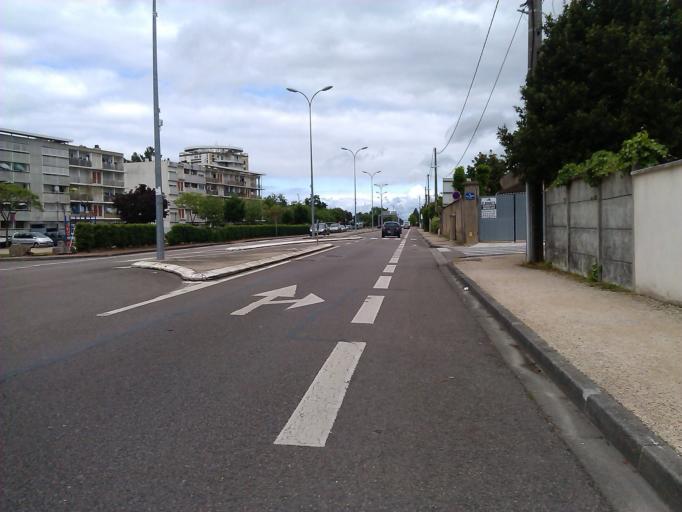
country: FR
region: Bourgogne
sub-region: Departement de Saone-et-Loire
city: Champforgeuil
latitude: 46.8044
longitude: 4.8451
